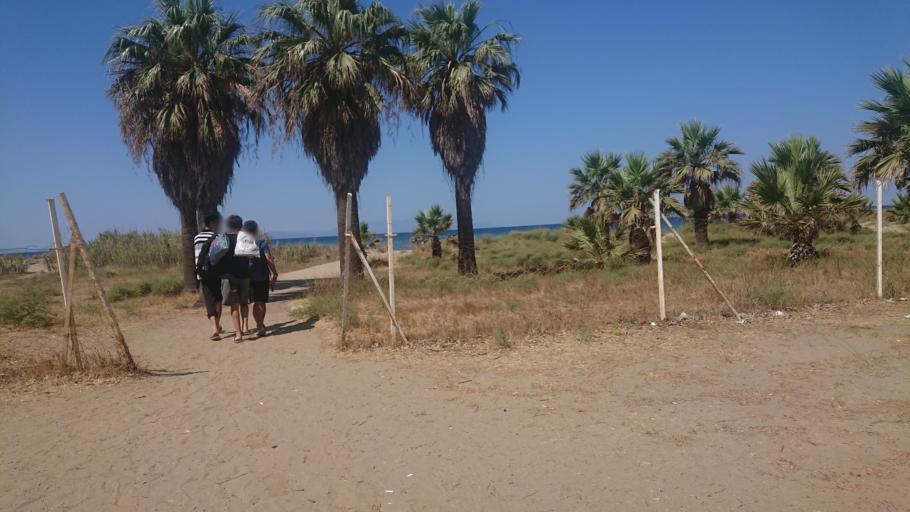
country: TR
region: Aydin
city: Kusadasi
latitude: 37.9388
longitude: 27.2761
